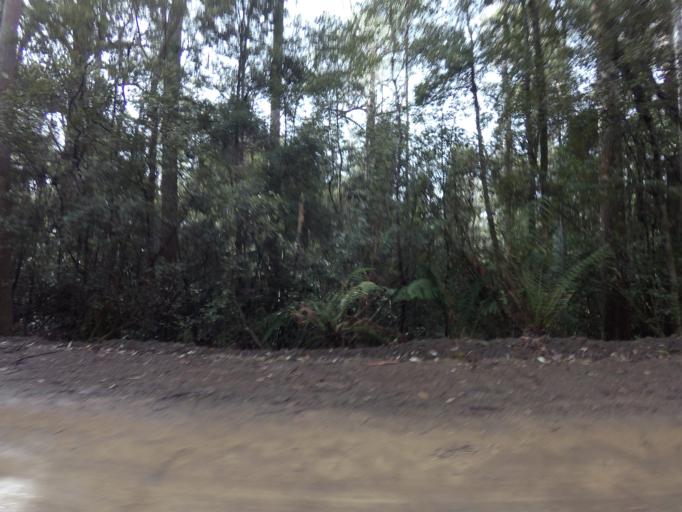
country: AU
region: Tasmania
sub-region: Huon Valley
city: Geeveston
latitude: -43.5734
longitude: 146.8884
